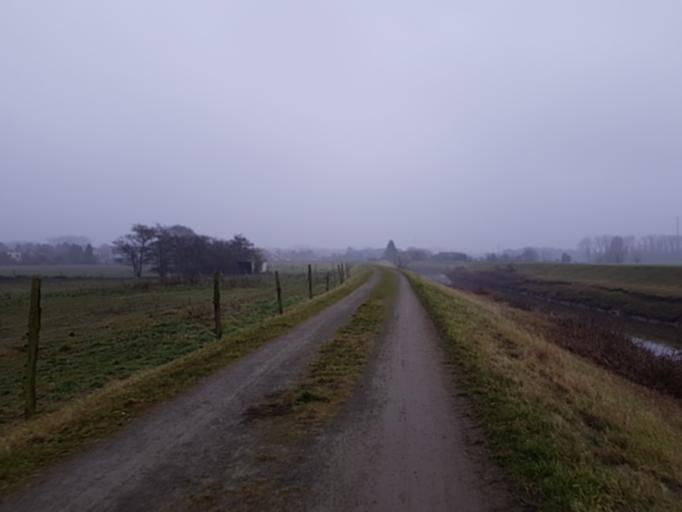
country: BE
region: Flanders
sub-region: Provincie Vlaams-Brabant
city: Haacht
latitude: 50.9901
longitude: 4.6401
